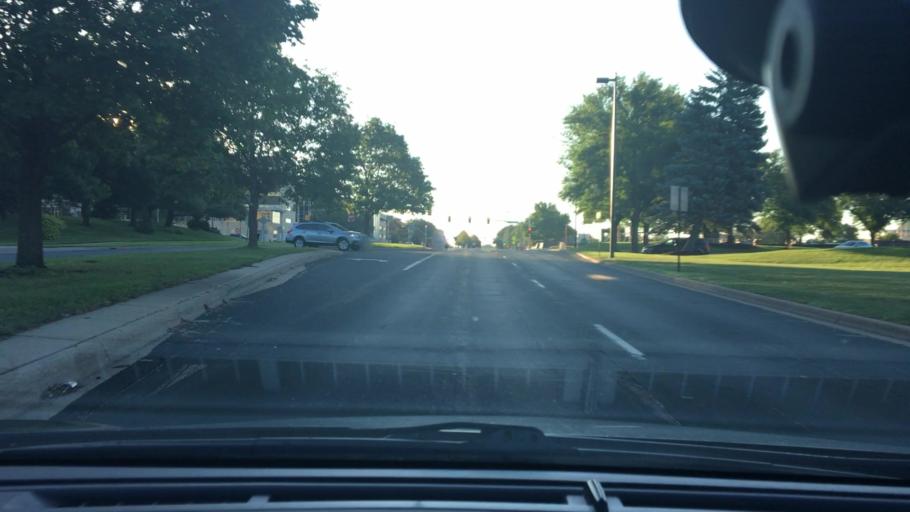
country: US
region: Minnesota
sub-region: Hennepin County
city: Edina
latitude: 44.8836
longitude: -93.3308
